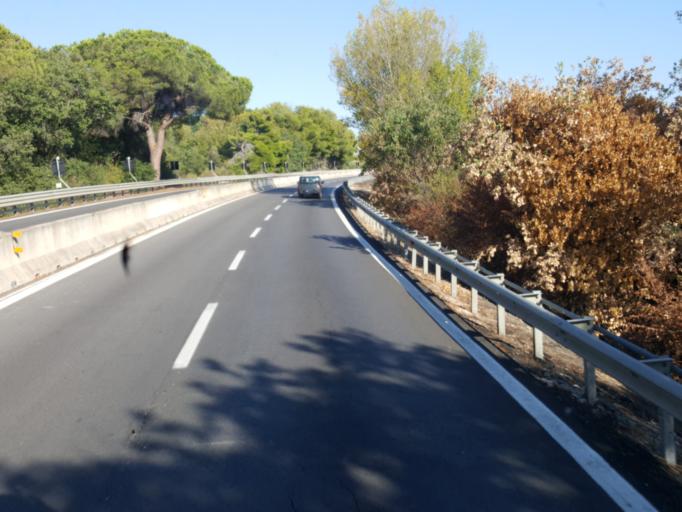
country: IT
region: Latium
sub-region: Provincia di Viterbo
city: Pescia Romana
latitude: 42.4137
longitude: 11.4733
